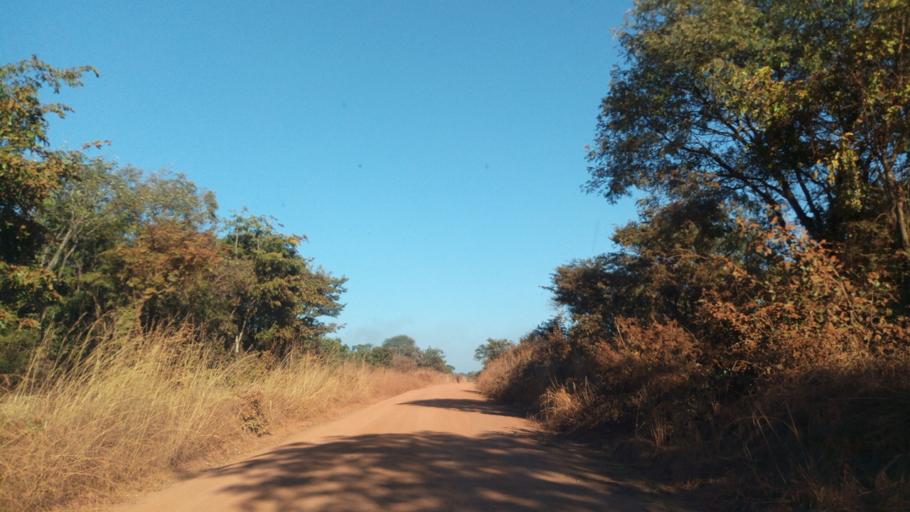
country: ZM
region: Luapula
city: Mwense
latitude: -10.4856
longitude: 28.4948
